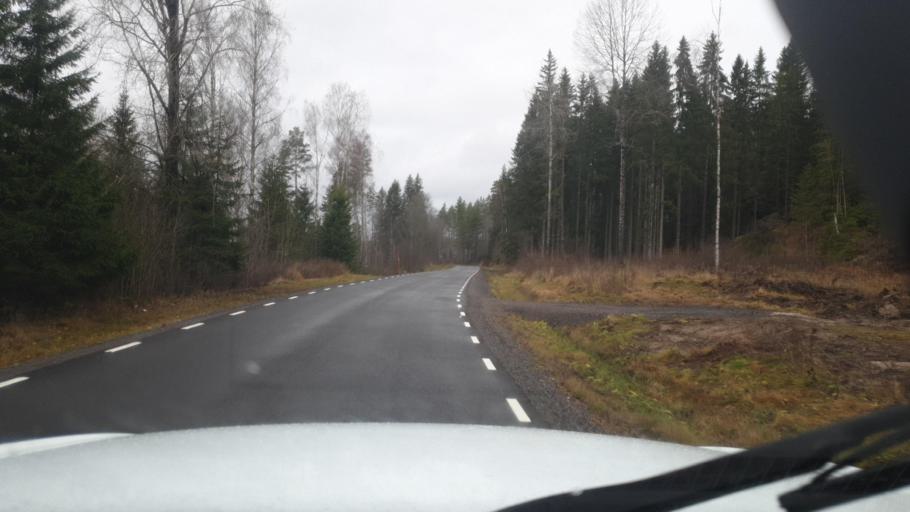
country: SE
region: Vaermland
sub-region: Eda Kommun
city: Amotfors
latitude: 59.8284
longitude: 12.4376
